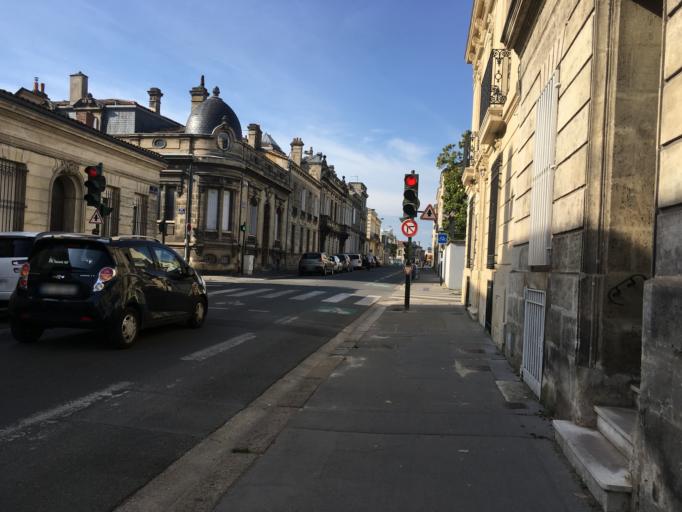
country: FR
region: Aquitaine
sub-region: Departement de la Gironde
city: Bordeaux
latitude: 44.8234
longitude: -0.5821
